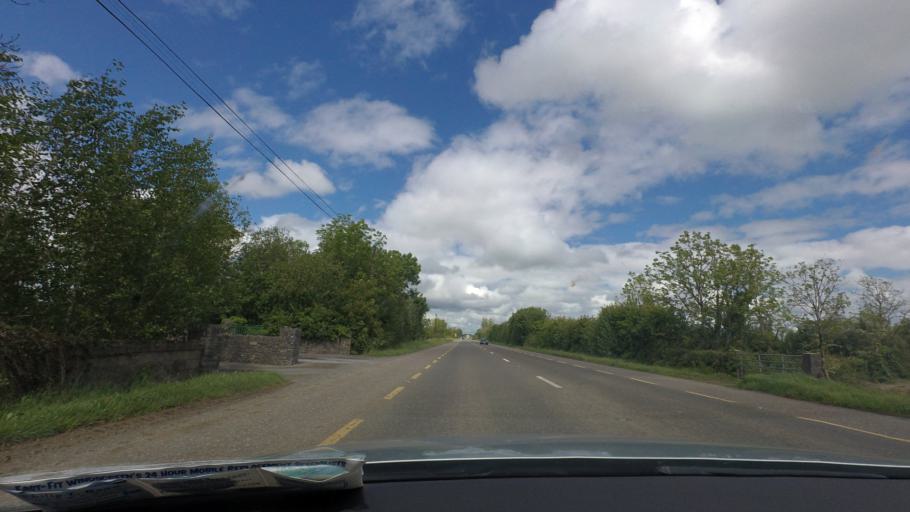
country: IE
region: Munster
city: Thurles
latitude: 52.6061
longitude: -7.7895
